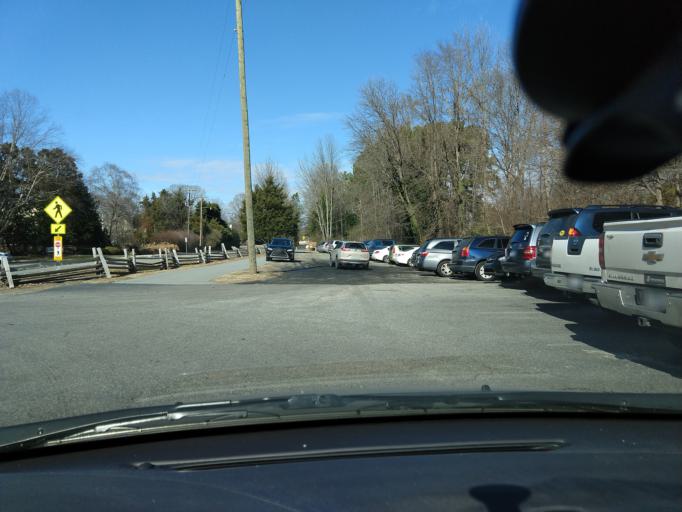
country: US
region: North Carolina
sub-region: Guilford County
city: Greensboro
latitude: 36.1342
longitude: -79.8461
